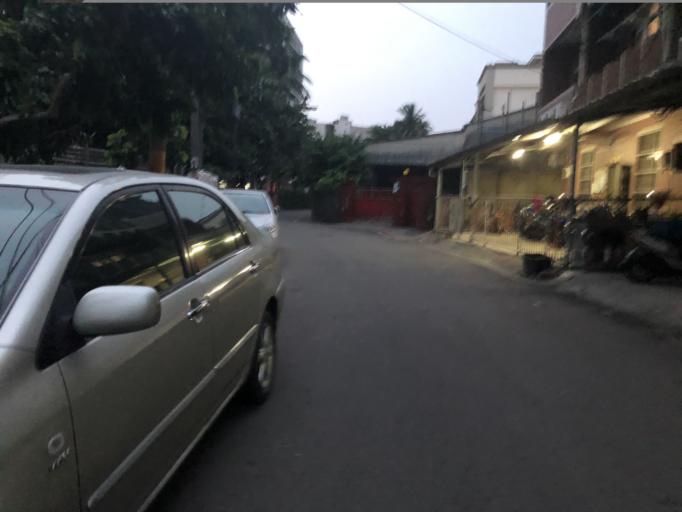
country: TW
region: Taiwan
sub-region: Tainan
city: Tainan
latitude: 23.0258
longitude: 120.2240
